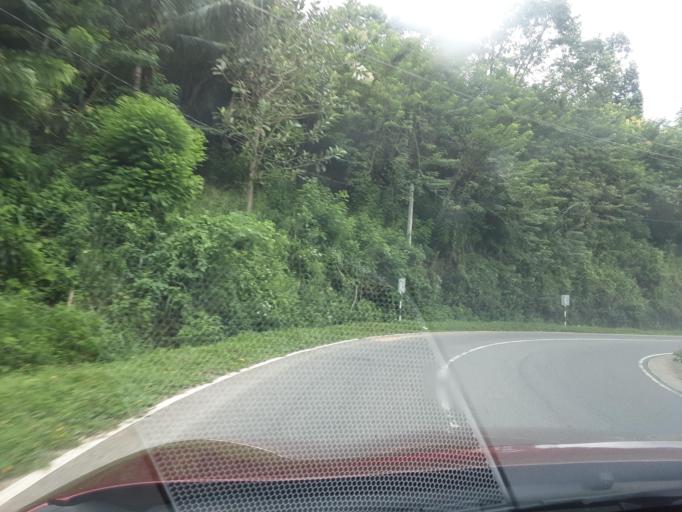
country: LK
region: Uva
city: Monaragala
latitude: 6.9096
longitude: 81.2127
